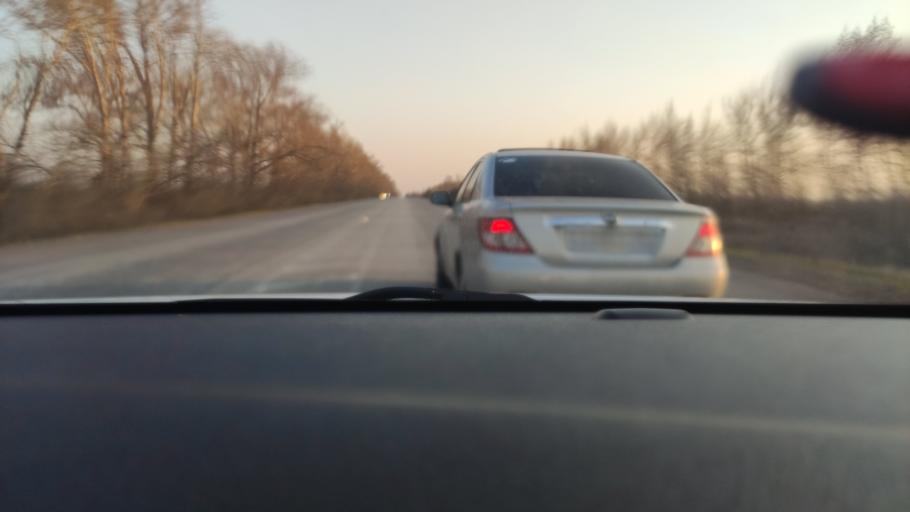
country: RU
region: Voronezj
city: Maslovka
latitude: 51.4703
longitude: 39.3057
